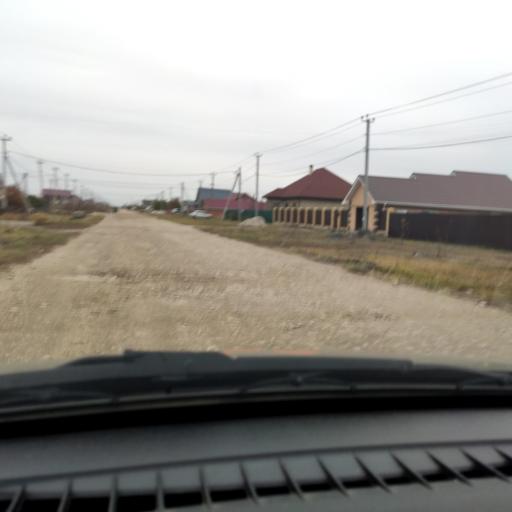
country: RU
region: Samara
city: Podstepki
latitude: 53.5256
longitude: 49.1542
